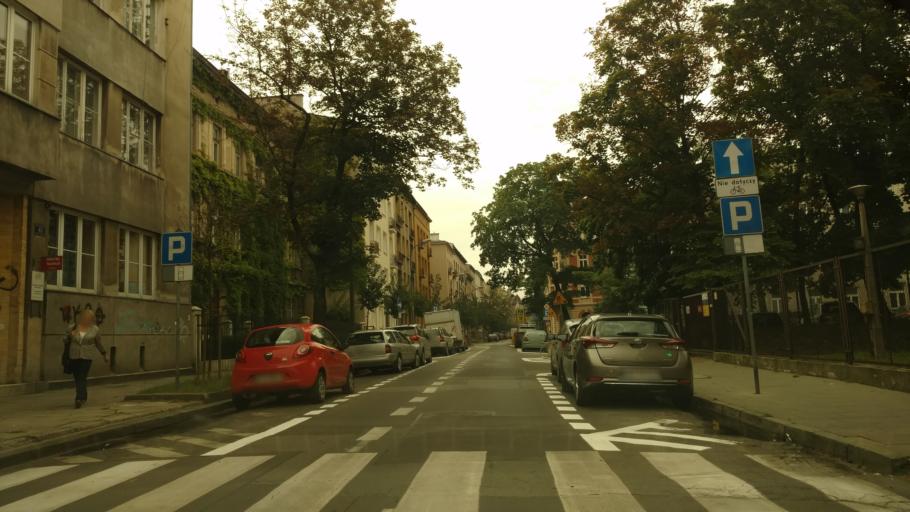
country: PL
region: Lesser Poland Voivodeship
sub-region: Krakow
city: Krakow
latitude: 50.0700
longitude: 19.9324
